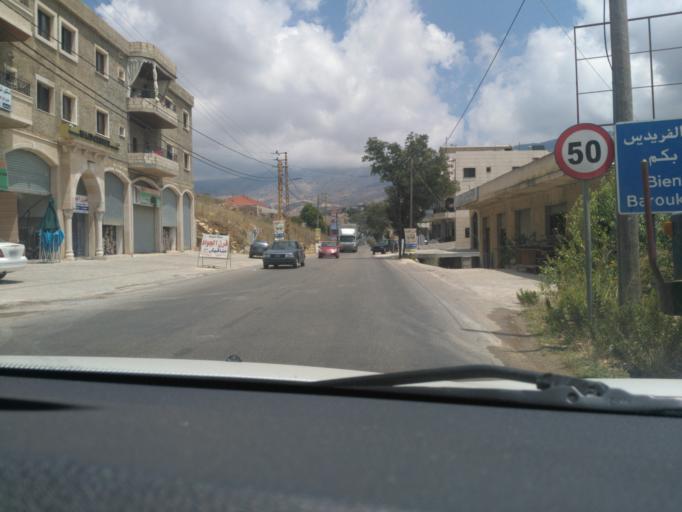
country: LB
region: Mont-Liban
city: Beit ed Dine
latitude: 33.7045
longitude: 35.6654
